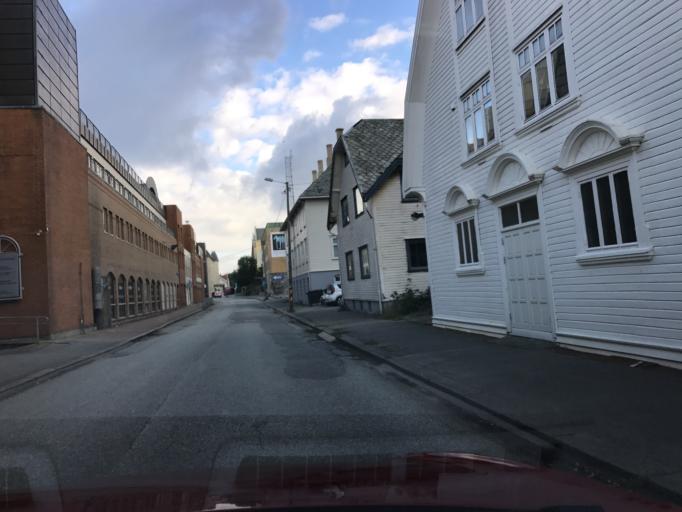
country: NO
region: Rogaland
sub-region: Haugesund
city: Haugesund
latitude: 59.4104
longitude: 5.2748
